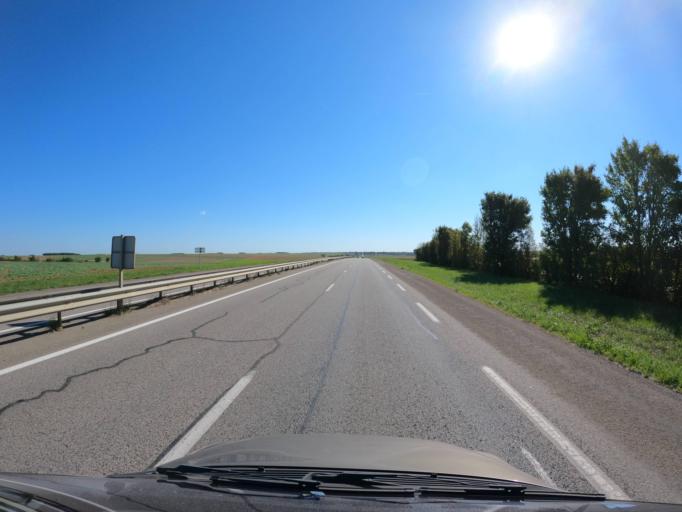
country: FR
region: Poitou-Charentes
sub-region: Departement de la Vienne
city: Vouille
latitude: 46.6504
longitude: 0.1348
